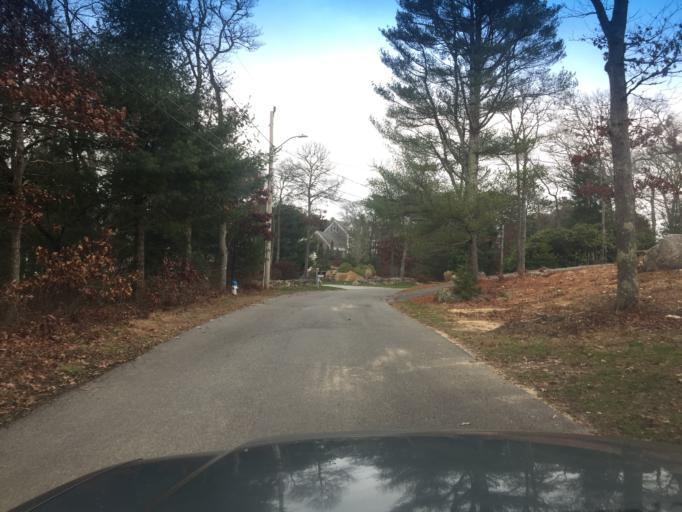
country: US
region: Massachusetts
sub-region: Barnstable County
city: North Falmouth
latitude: 41.6388
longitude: -70.6147
